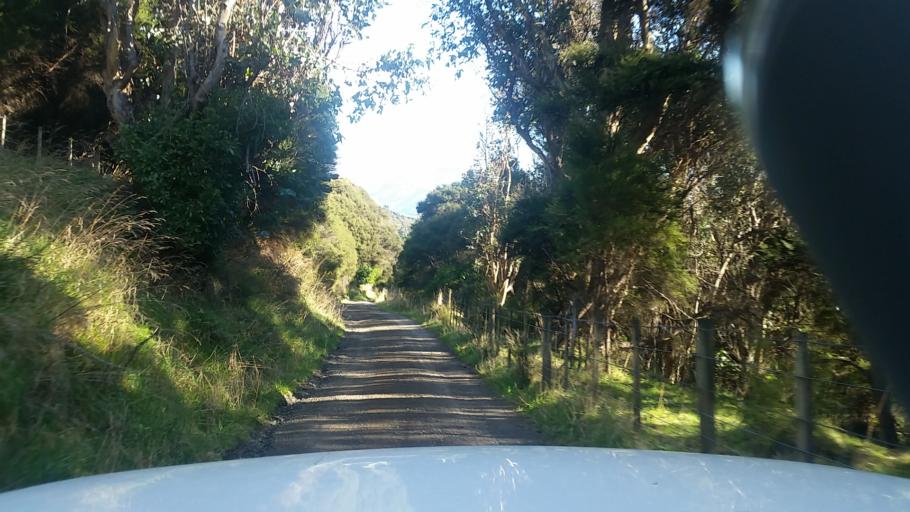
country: NZ
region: Canterbury
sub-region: Christchurch City
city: Christchurch
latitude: -43.7925
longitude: 172.9962
